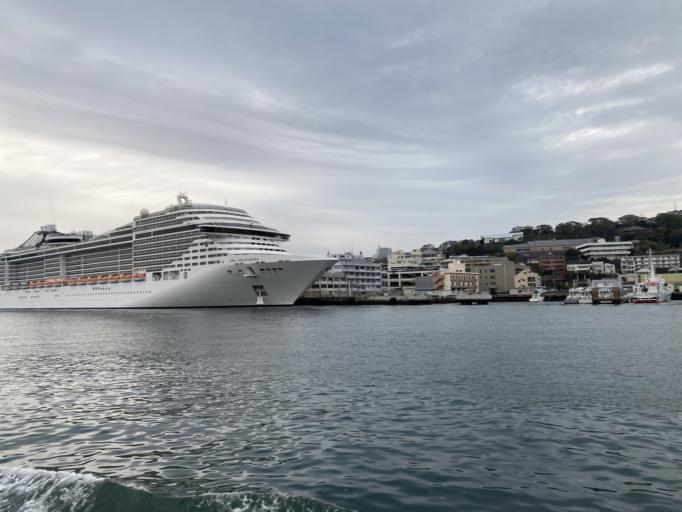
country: JP
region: Nagasaki
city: Nagasaki-shi
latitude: 32.7353
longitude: 129.8639
